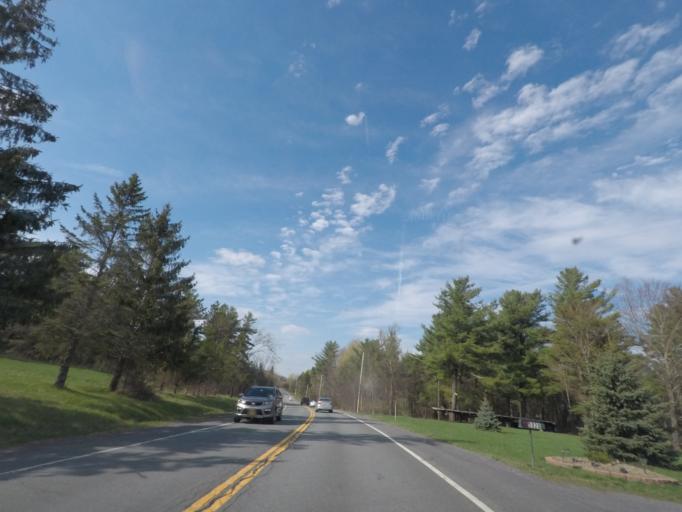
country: US
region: New York
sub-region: Albany County
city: Voorheesville
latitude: 42.6073
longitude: -73.9712
